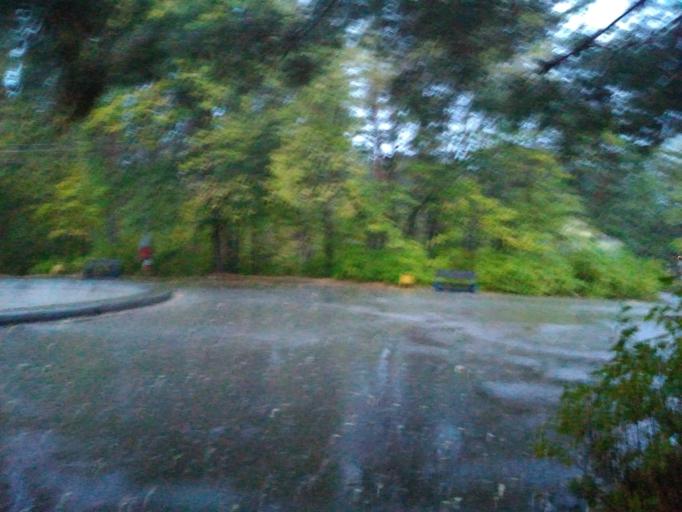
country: RU
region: Ulyanovsk
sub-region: Ulyanovskiy Rayon
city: Ulyanovsk
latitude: 54.3615
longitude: 48.5154
